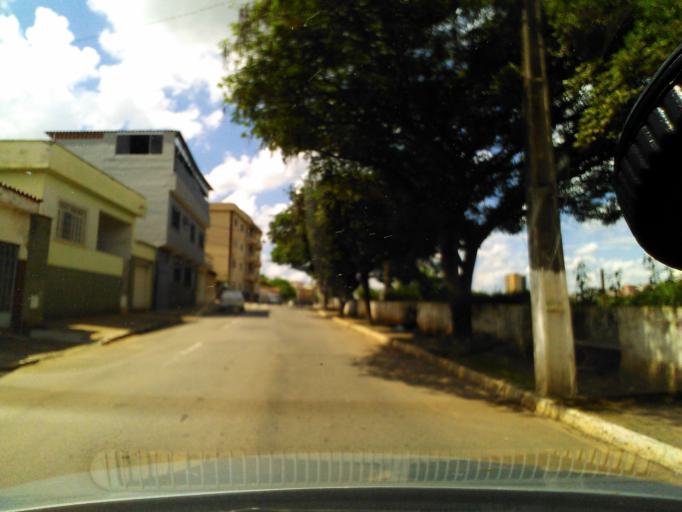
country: BR
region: Minas Gerais
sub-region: Tres Coracoes
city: Tres Coracoes
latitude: -21.7028
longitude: -45.2603
